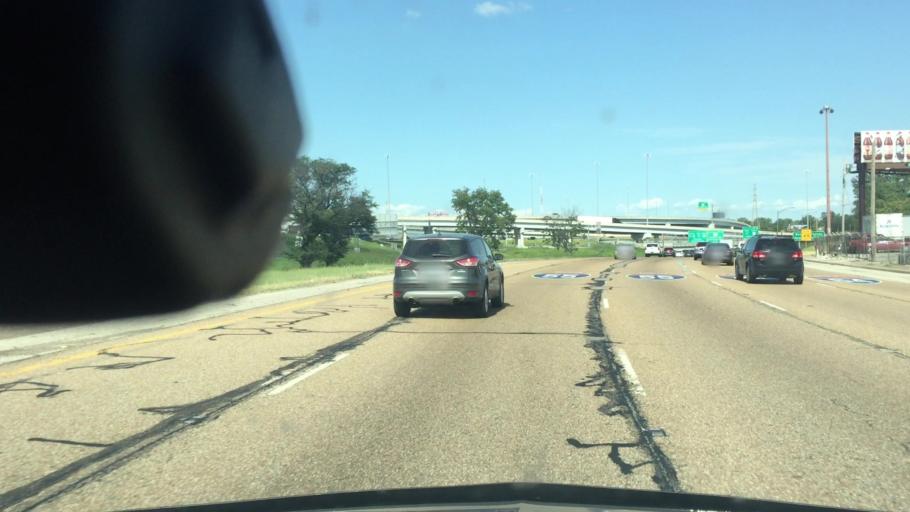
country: US
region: Illinois
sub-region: Saint Clair County
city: East Saint Louis
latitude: 38.6321
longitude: -90.1497
